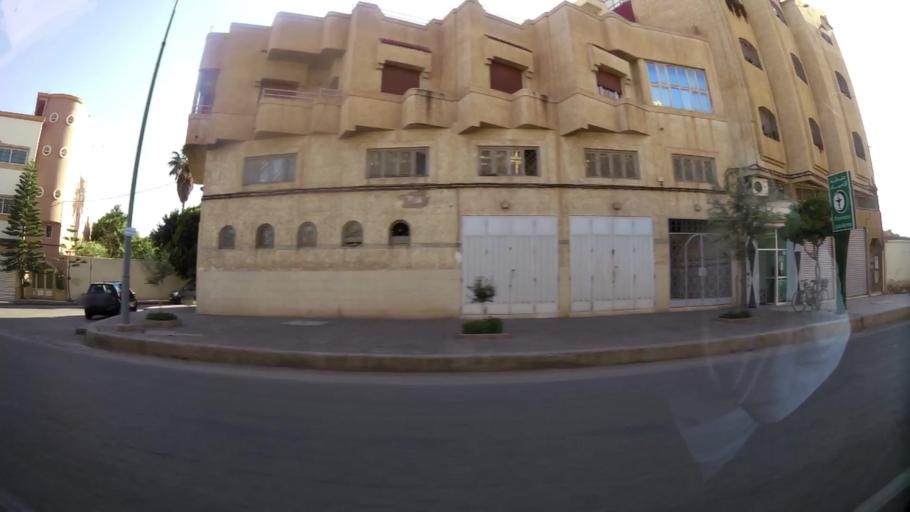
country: MA
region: Oriental
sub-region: Oujda-Angad
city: Oujda
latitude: 34.6948
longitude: -1.9087
